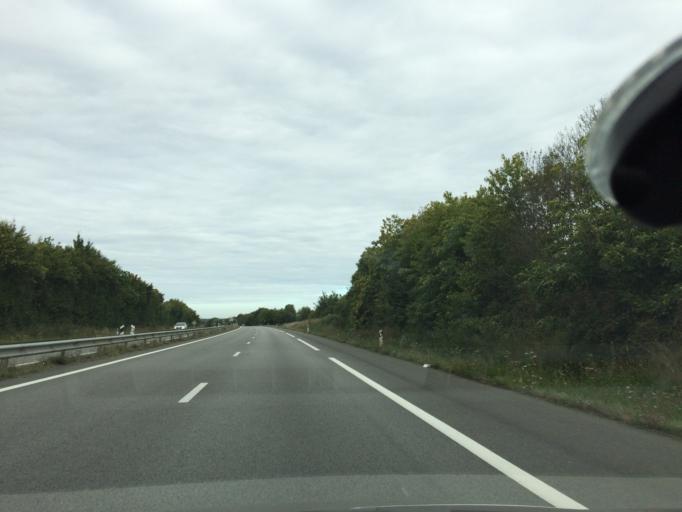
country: FR
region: Brittany
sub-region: Departement d'Ille-et-Vilaine
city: Saint-Domineuc
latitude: 48.3586
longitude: -1.8699
